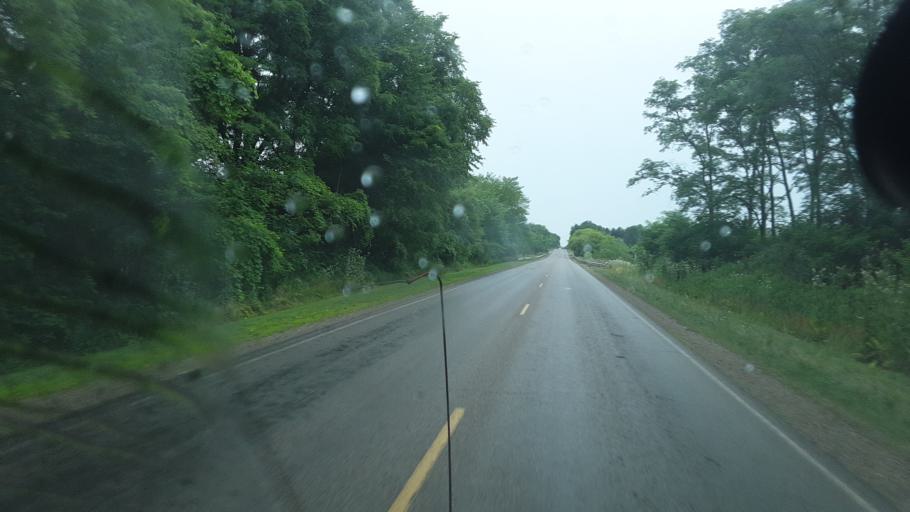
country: US
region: Michigan
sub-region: Hillsdale County
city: Reading
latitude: 41.7079
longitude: -84.7685
